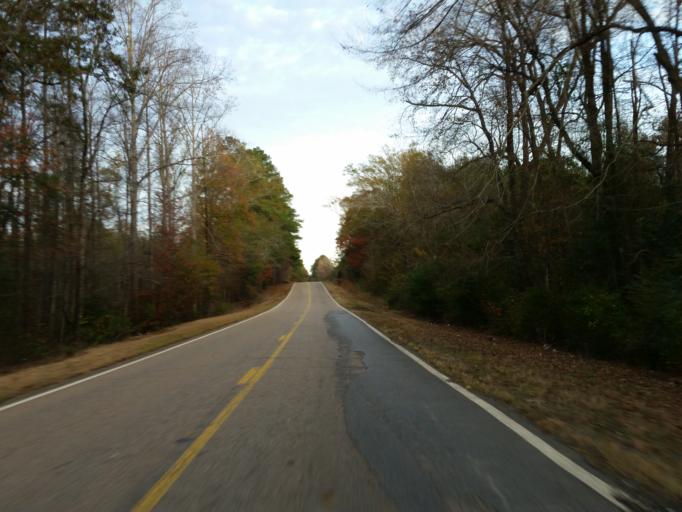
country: US
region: Alabama
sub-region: Sumter County
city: York
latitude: 32.4239
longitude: -88.4232
